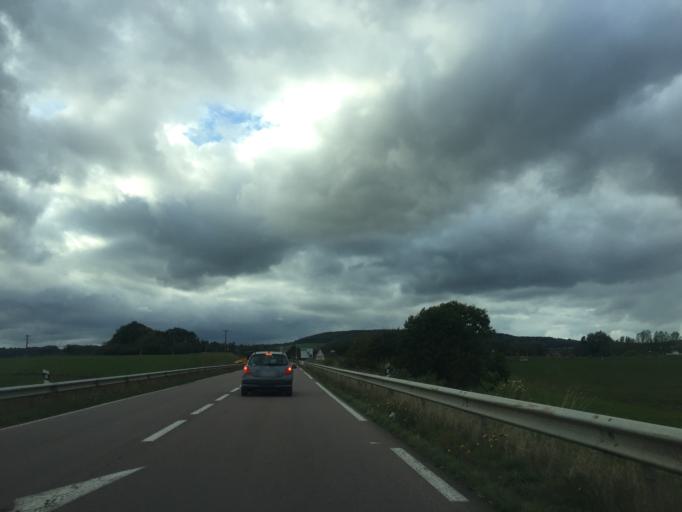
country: FR
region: Lorraine
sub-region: Departement des Vosges
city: Chatenois
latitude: 48.2968
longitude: 5.8559
